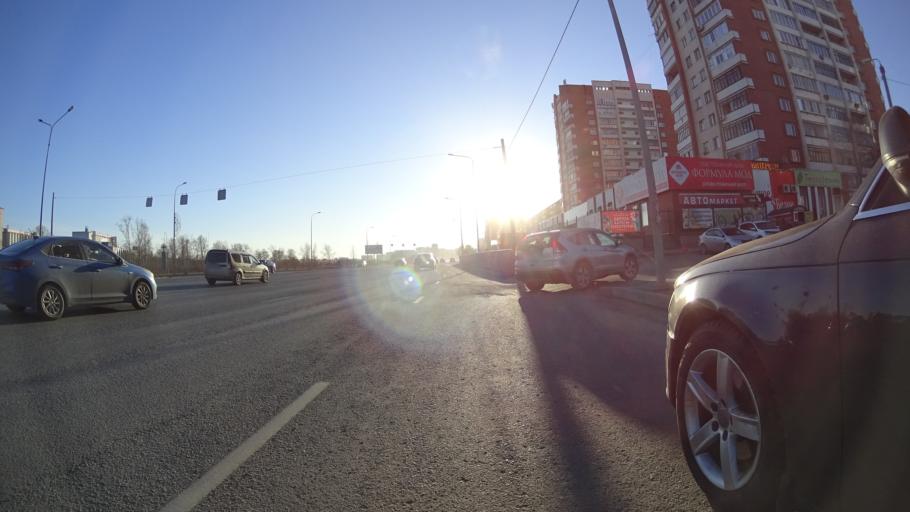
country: RU
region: Chelyabinsk
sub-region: Gorod Chelyabinsk
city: Chelyabinsk
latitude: 55.1746
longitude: 61.3476
